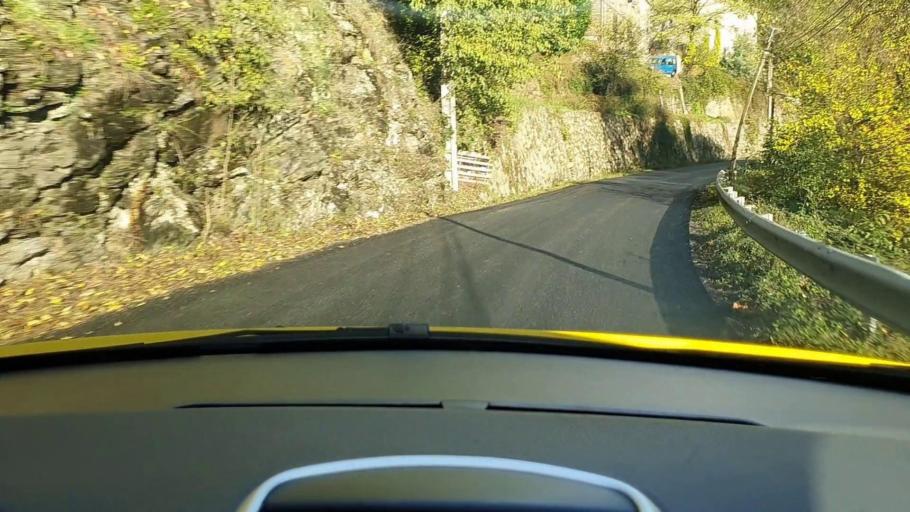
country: FR
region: Languedoc-Roussillon
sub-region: Departement du Gard
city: Sumene
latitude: 44.0053
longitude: 3.7091
